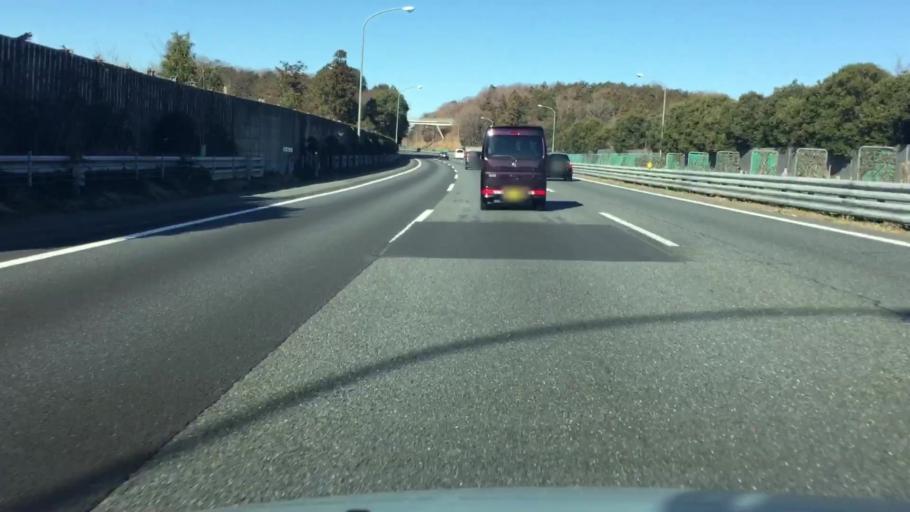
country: JP
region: Saitama
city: Ogawa
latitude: 36.0534
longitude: 139.3396
